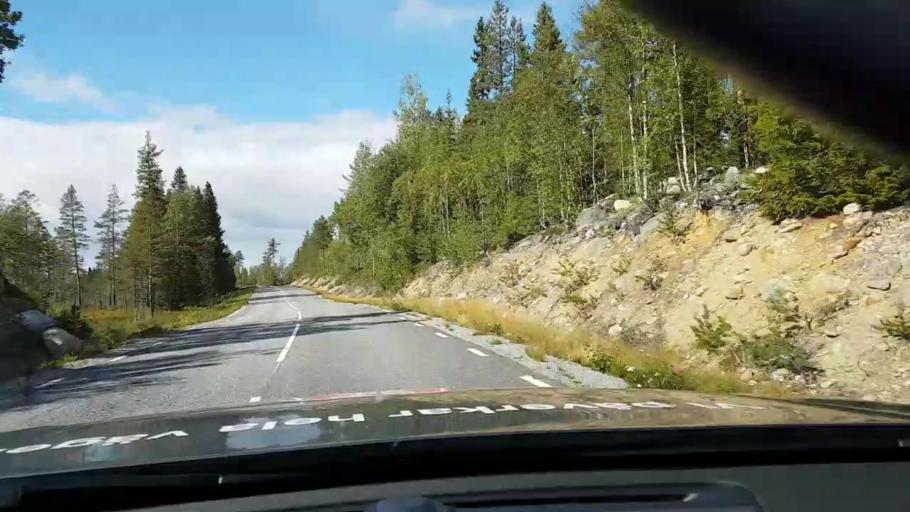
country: SE
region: Vaesterbotten
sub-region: Asele Kommun
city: Asele
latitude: 63.8323
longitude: 17.4512
